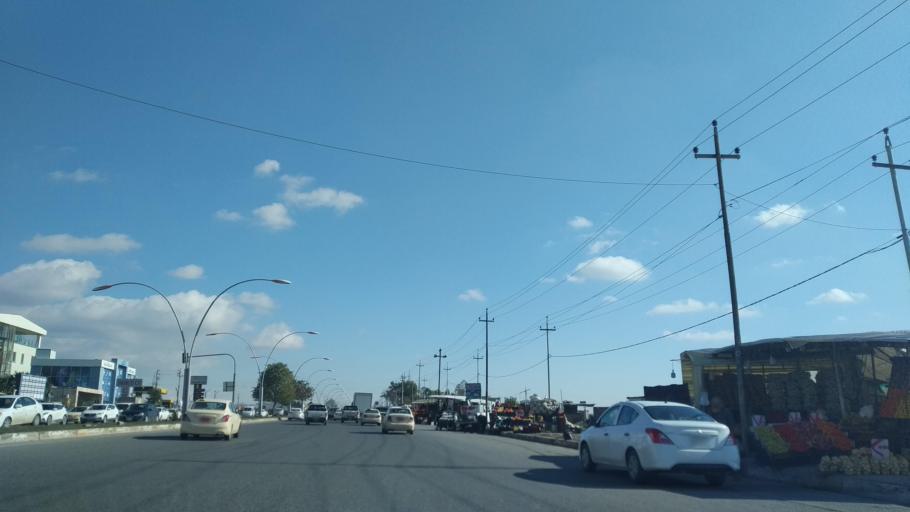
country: IQ
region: Arbil
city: Erbil
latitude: 36.1989
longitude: 44.0801
